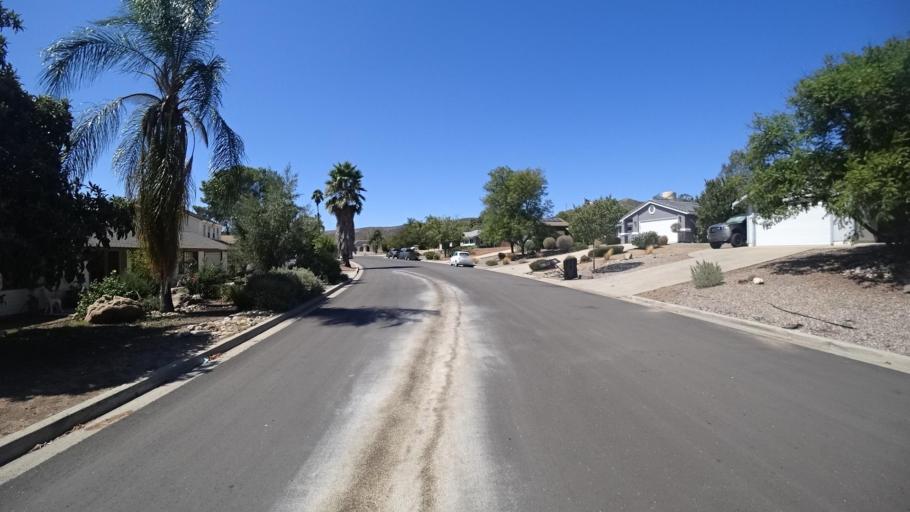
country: US
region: California
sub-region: San Diego County
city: San Diego Country Estates
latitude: 33.0203
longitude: -116.8082
